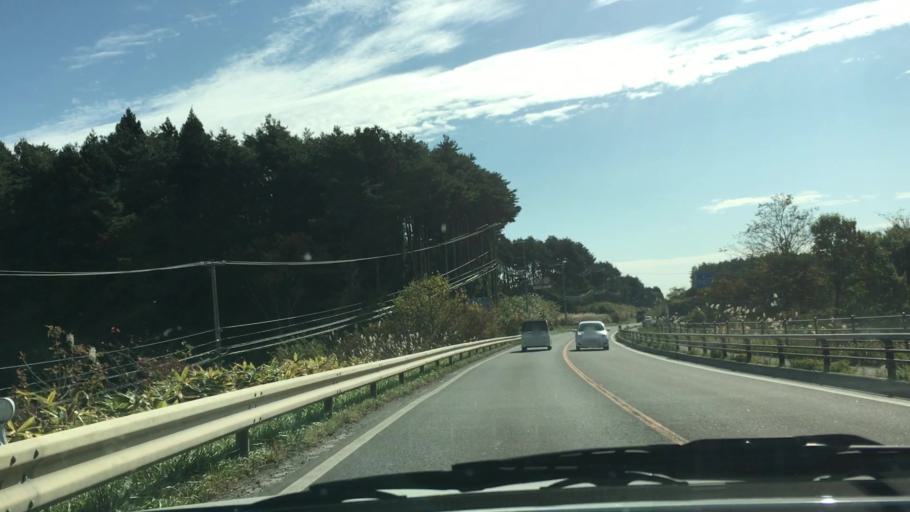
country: JP
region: Aomori
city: Hachinohe
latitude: 40.4368
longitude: 141.6856
